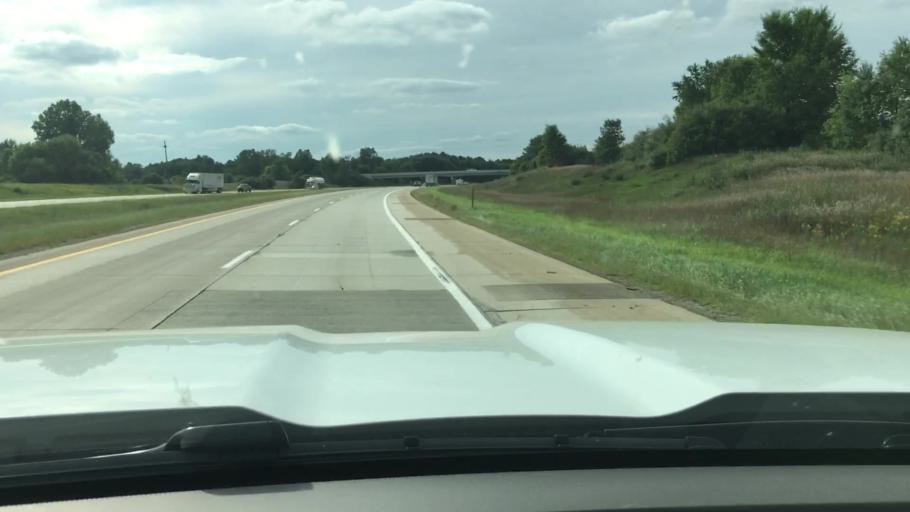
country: US
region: Michigan
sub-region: Lapeer County
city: Lapeer
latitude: 43.0120
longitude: -83.2762
